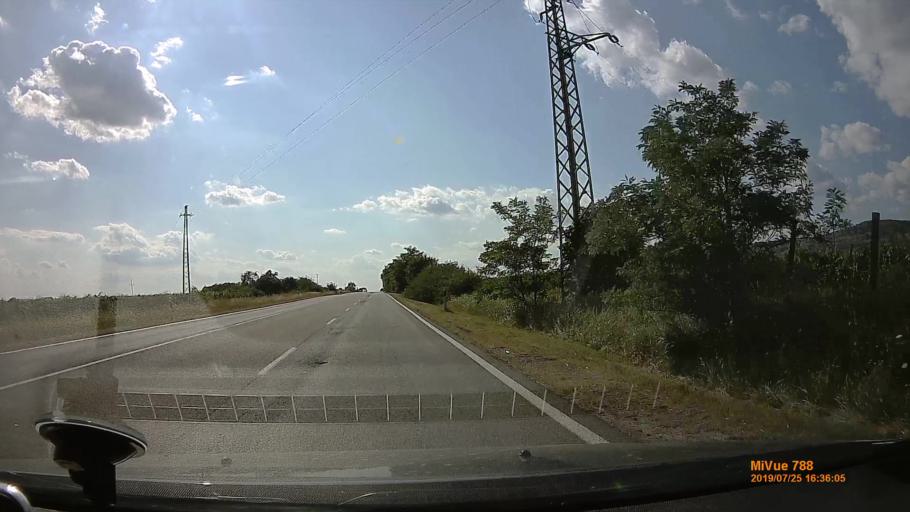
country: HU
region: Heves
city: Abasar
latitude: 47.7683
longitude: 19.9895
